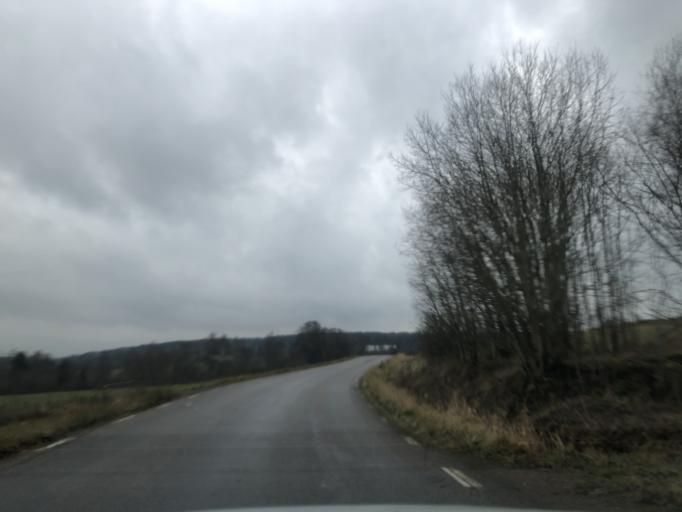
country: SE
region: Vaestra Goetaland
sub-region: Ulricehamns Kommun
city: Ulricehamn
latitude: 57.8890
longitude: 13.5115
